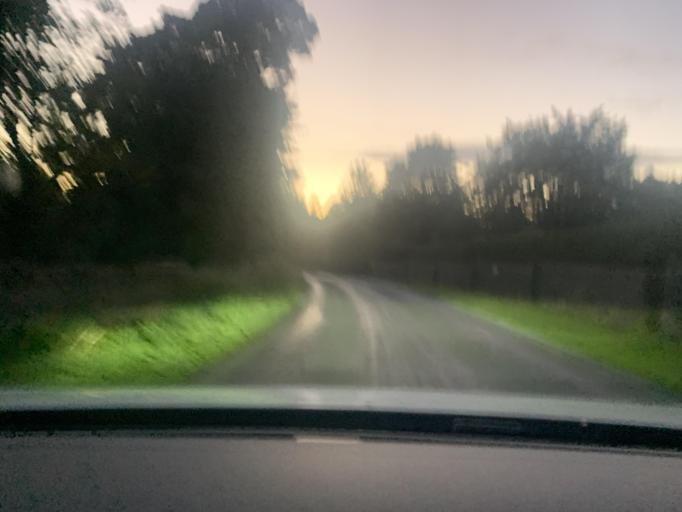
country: IE
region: Connaught
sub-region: Sligo
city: Sligo
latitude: 54.2831
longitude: -8.4127
